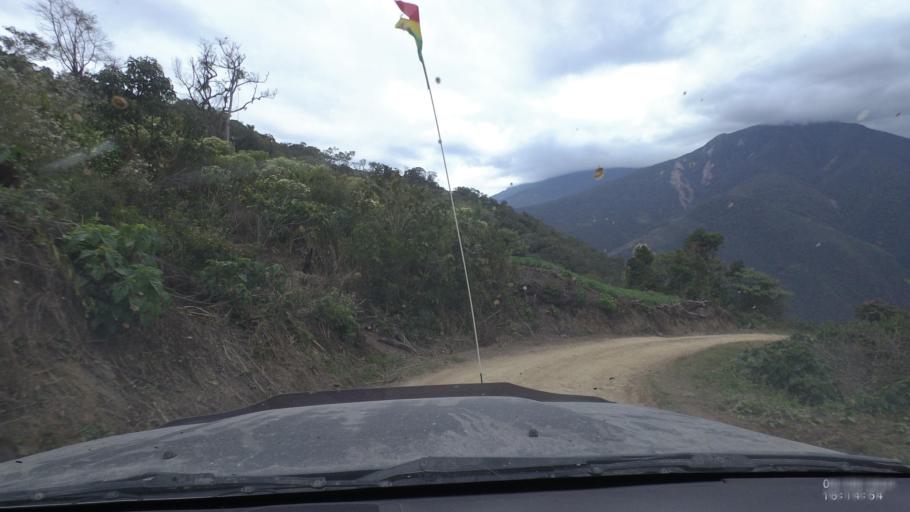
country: BO
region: La Paz
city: Quime
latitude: -16.5519
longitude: -66.7367
